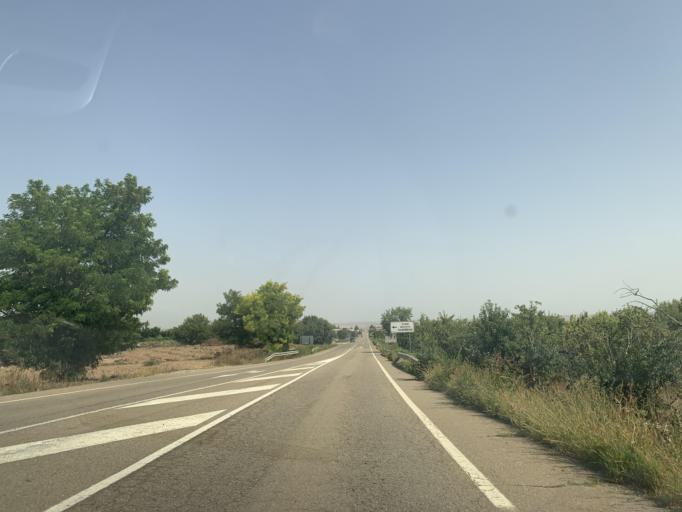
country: ES
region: Aragon
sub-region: Provincia de Zaragoza
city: Belchite
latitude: 41.3005
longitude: -0.7439
